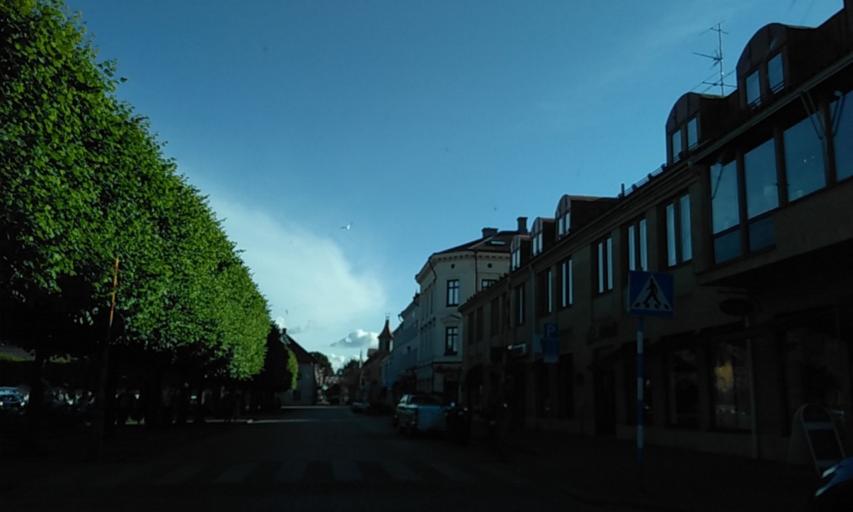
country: SE
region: Vaestra Goetaland
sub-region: Lidkopings Kommun
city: Lidkoping
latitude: 58.5045
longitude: 13.1571
